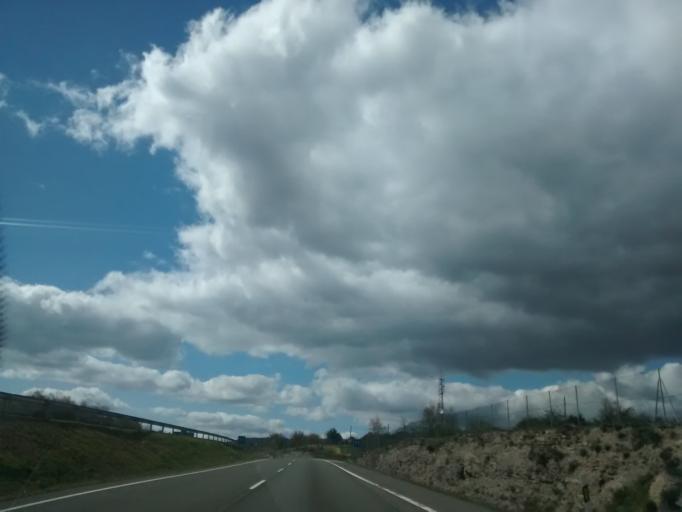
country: ES
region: Basque Country
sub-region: Provincia de Alava
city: Murguia
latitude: 42.9274
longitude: -2.7341
